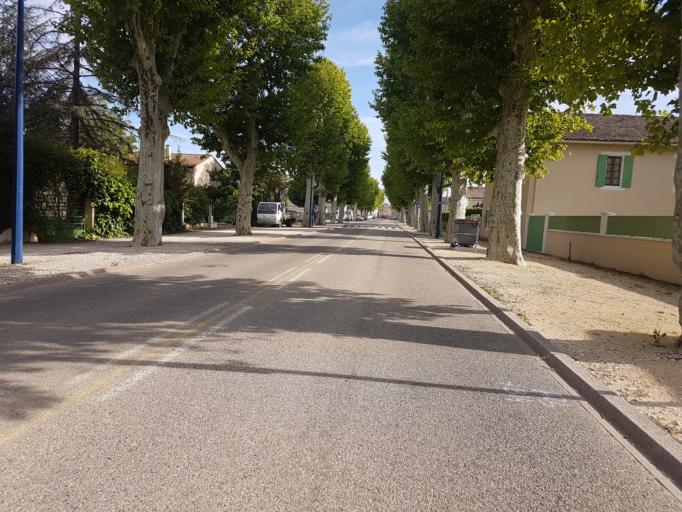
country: FR
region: Provence-Alpes-Cote d'Azur
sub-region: Departement du Vaucluse
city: Lapalud
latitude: 44.3097
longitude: 4.6858
